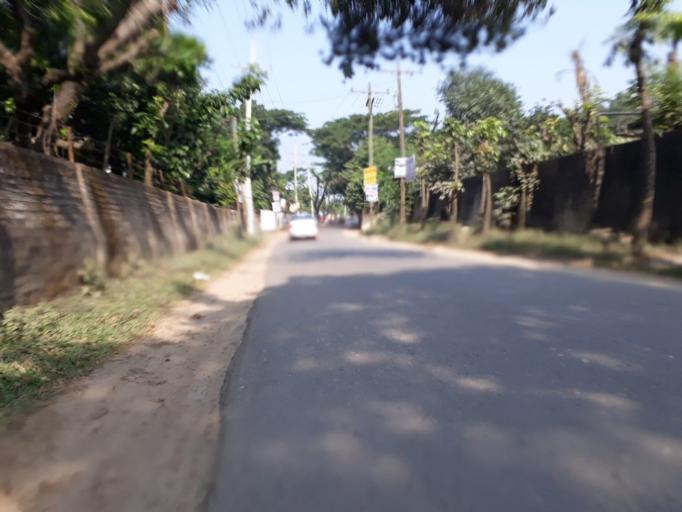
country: BD
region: Dhaka
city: Tungi
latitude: 23.8716
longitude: 90.3099
